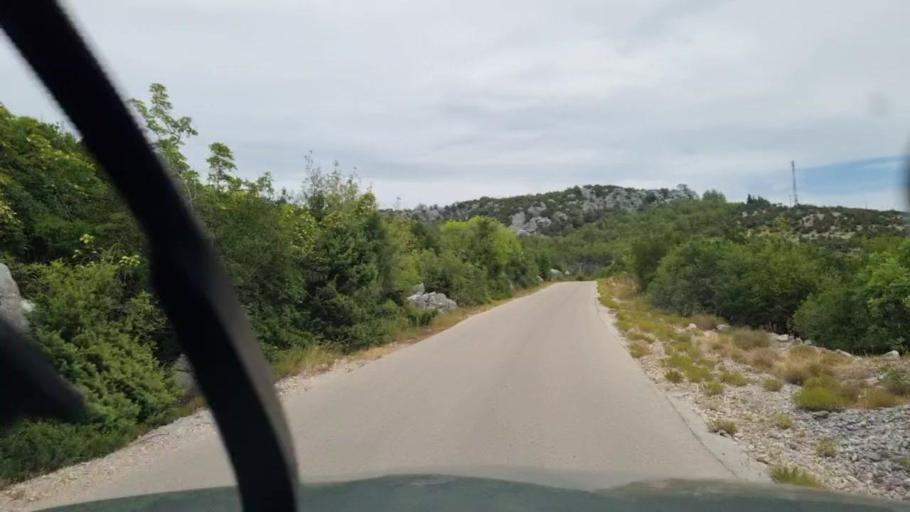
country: BA
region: Federation of Bosnia and Herzegovina
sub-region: Hercegovacko-Bosanski Kanton
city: Neum
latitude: 42.9323
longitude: 17.6823
